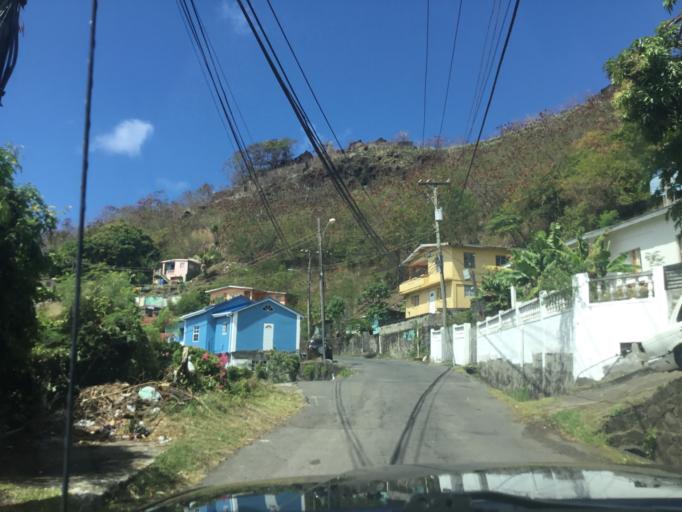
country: VC
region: Saint George
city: Kingstown Park
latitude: 13.1612
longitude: -61.2364
